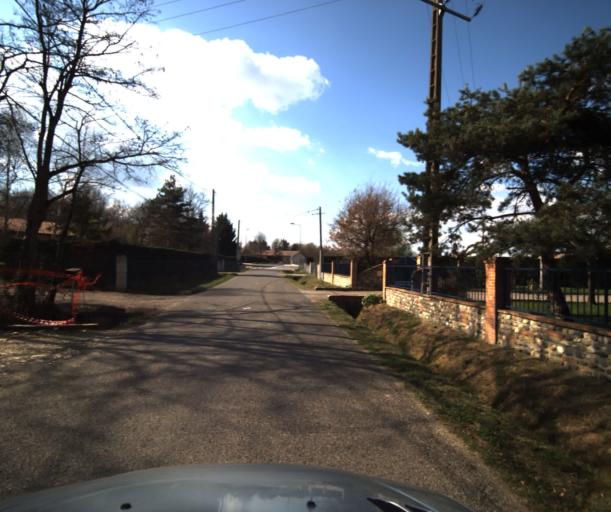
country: FR
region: Midi-Pyrenees
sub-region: Departement du Tarn-et-Garonne
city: Montbeton
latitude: 43.9758
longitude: 1.2847
